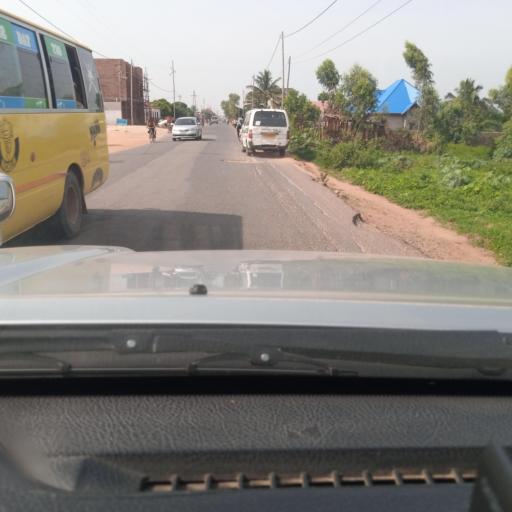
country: BI
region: Bujumbura Mairie
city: Bujumbura
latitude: -3.4562
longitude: 29.3513
